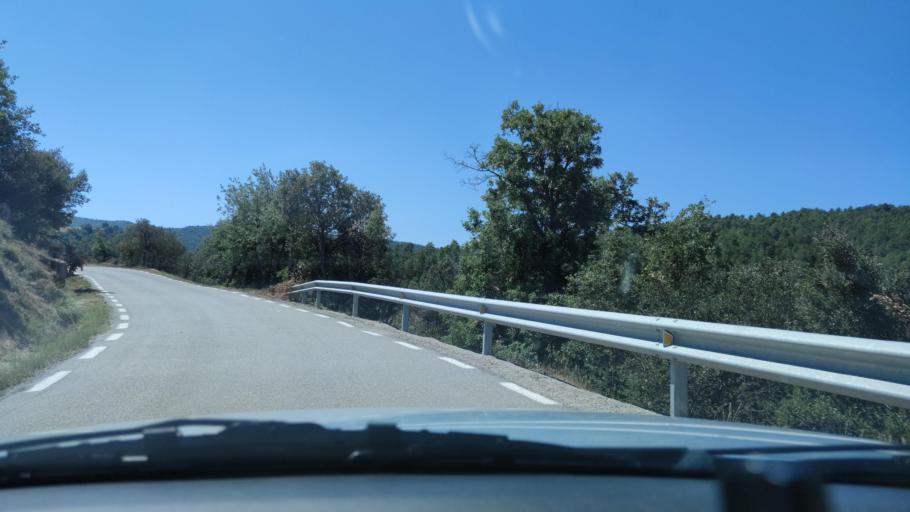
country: ES
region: Catalonia
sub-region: Provincia de Lleida
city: Tora de Riubregos
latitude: 41.8336
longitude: 1.4219
